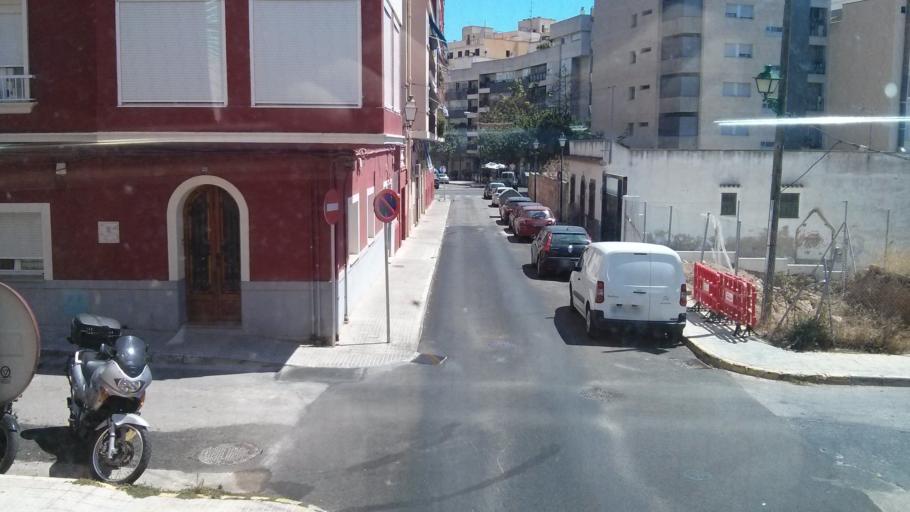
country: ES
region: Balearic Islands
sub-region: Illes Balears
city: Palma
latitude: 39.5721
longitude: 2.6301
